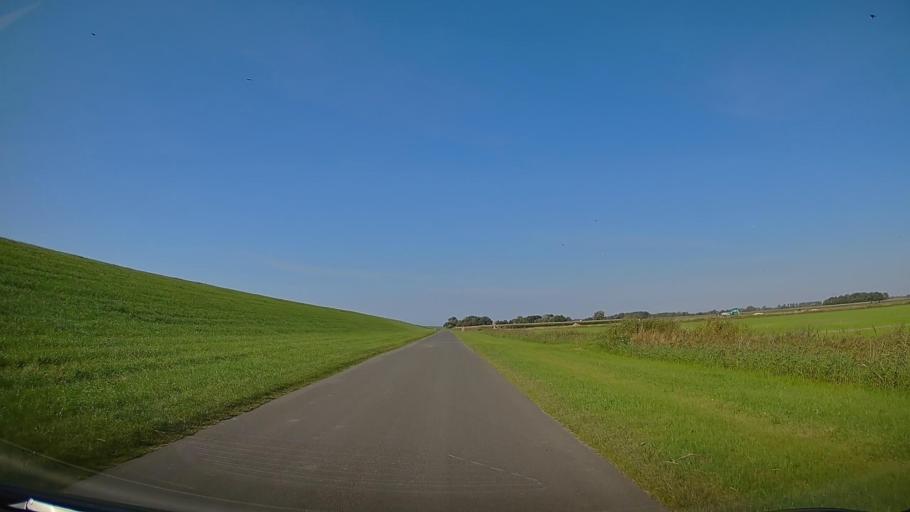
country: DE
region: Lower Saxony
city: Misselwarden
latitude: 53.6641
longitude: 8.4883
